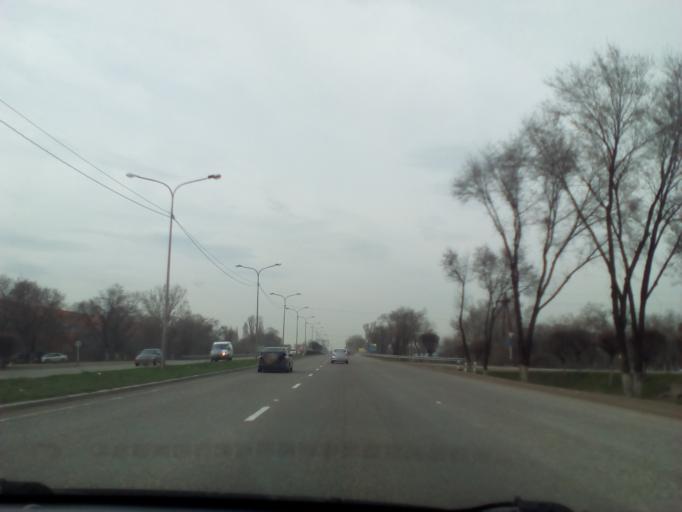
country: KZ
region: Almaty Oblysy
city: Burunday
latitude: 43.2185
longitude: 76.6465
